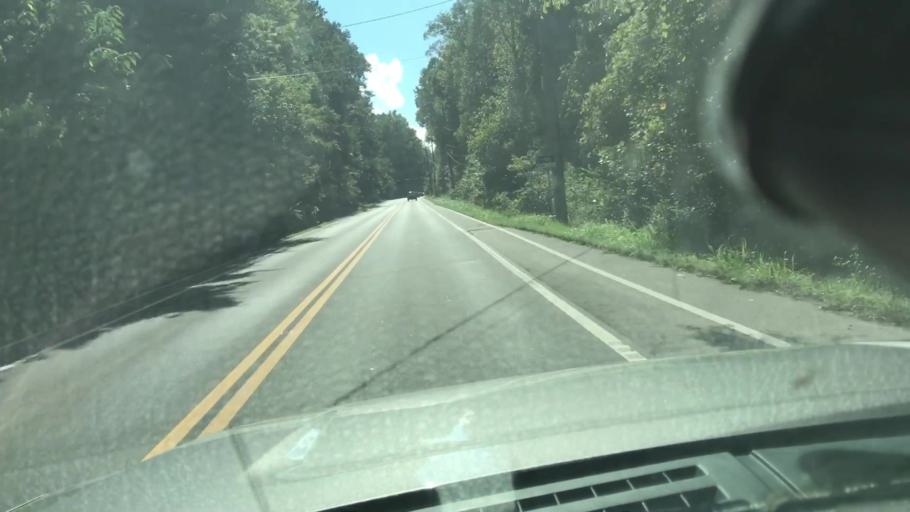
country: US
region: Tennessee
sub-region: Cheatham County
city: Pegram
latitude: 36.0341
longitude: -86.9831
